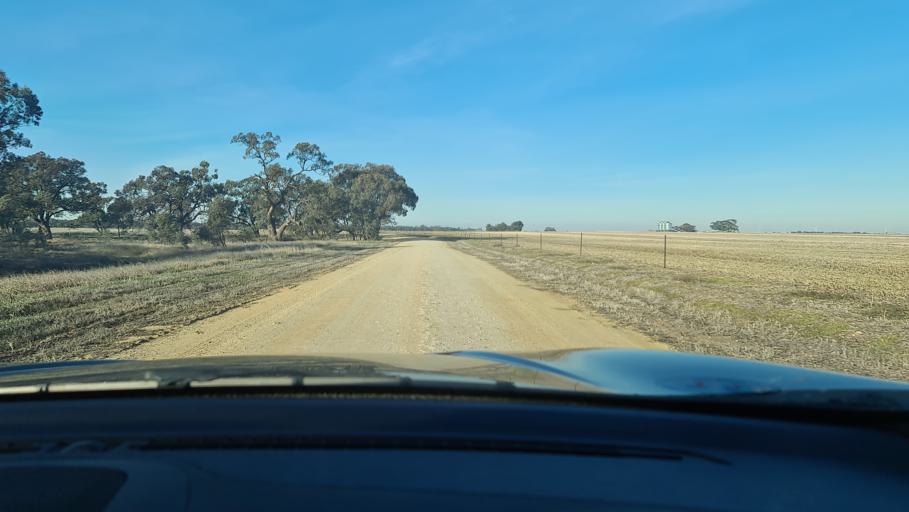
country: AU
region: Victoria
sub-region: Horsham
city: Horsham
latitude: -36.3586
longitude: 142.3963
